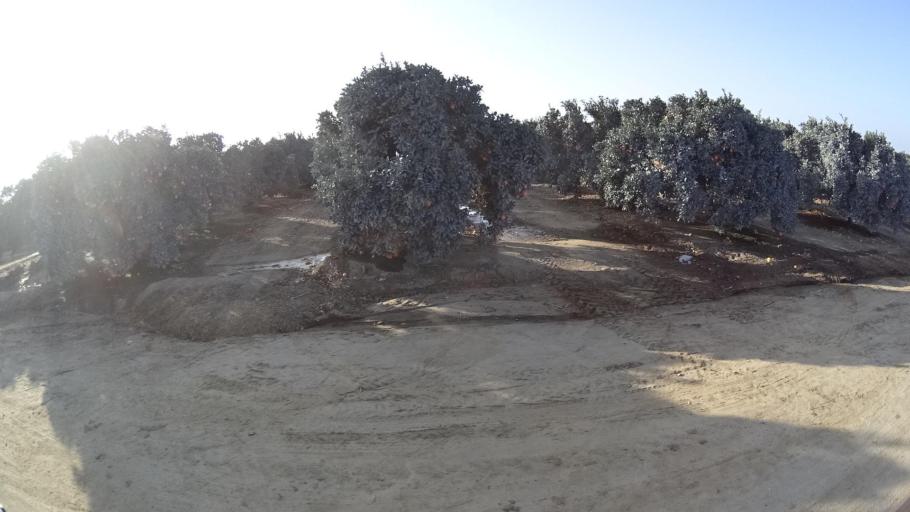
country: US
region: California
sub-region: Tulare County
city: Richgrove
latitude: 35.7763
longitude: -119.0898
